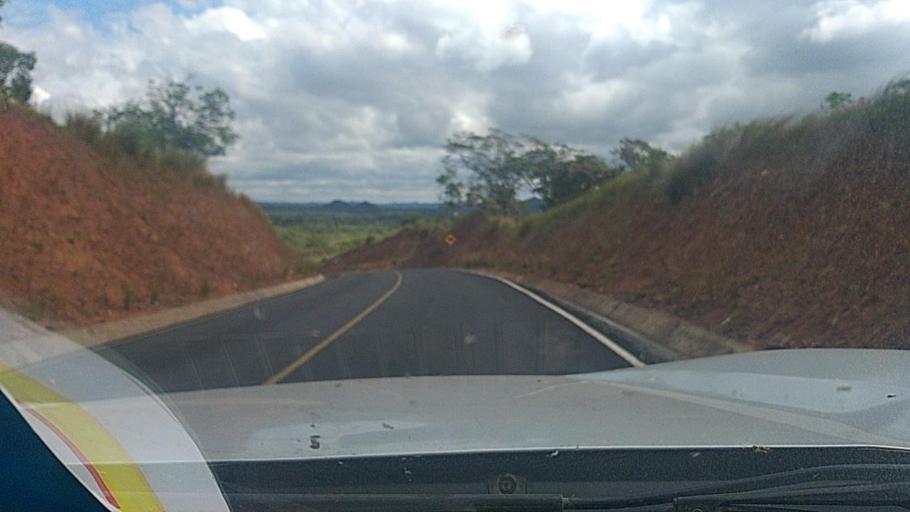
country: NI
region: Atlantico Sur
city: Muelle de los Bueyes
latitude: 12.1294
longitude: -84.4337
